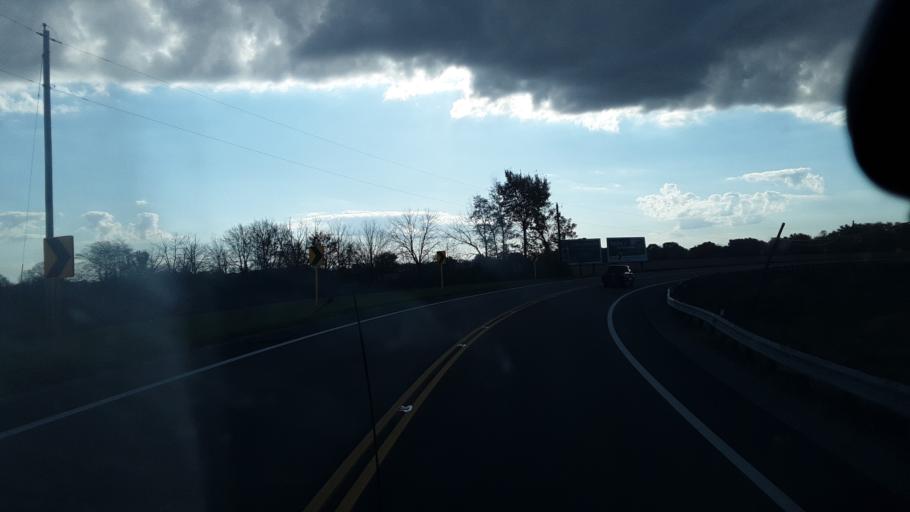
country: US
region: Ohio
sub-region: Fayette County
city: Washington Court House
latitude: 39.5600
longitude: -83.4530
